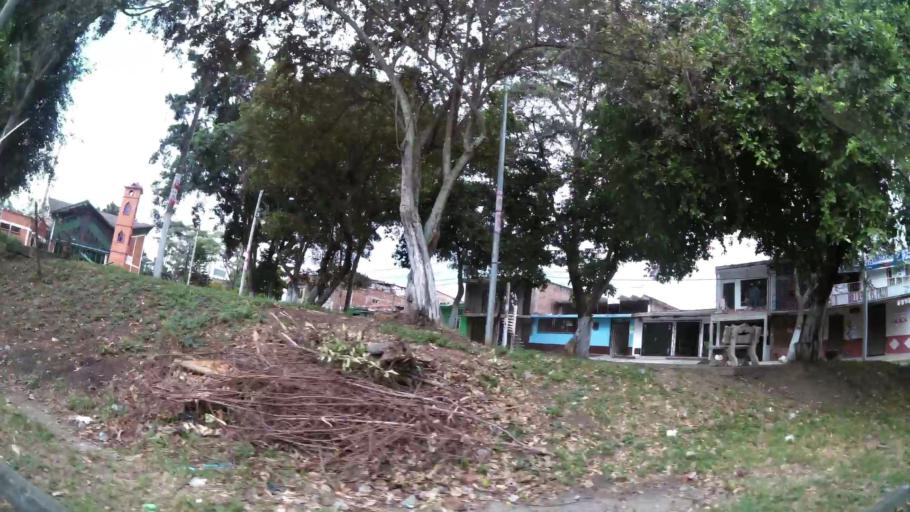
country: CO
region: Valle del Cauca
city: Cali
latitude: 3.4948
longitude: -76.4891
